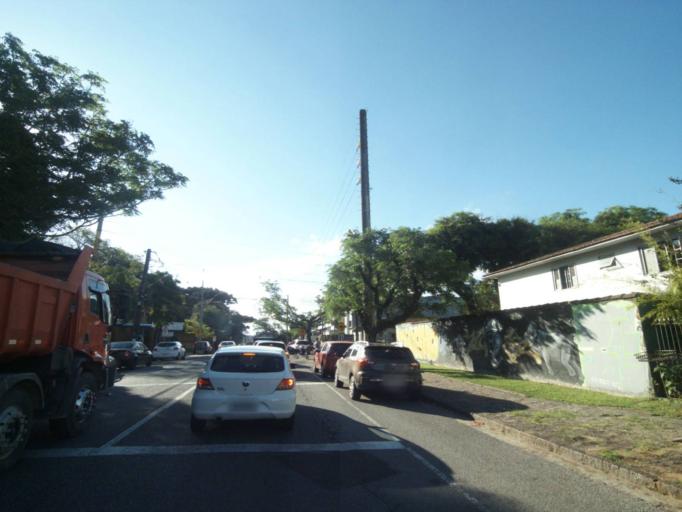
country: BR
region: Parana
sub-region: Curitiba
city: Curitiba
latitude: -25.3976
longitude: -49.2481
